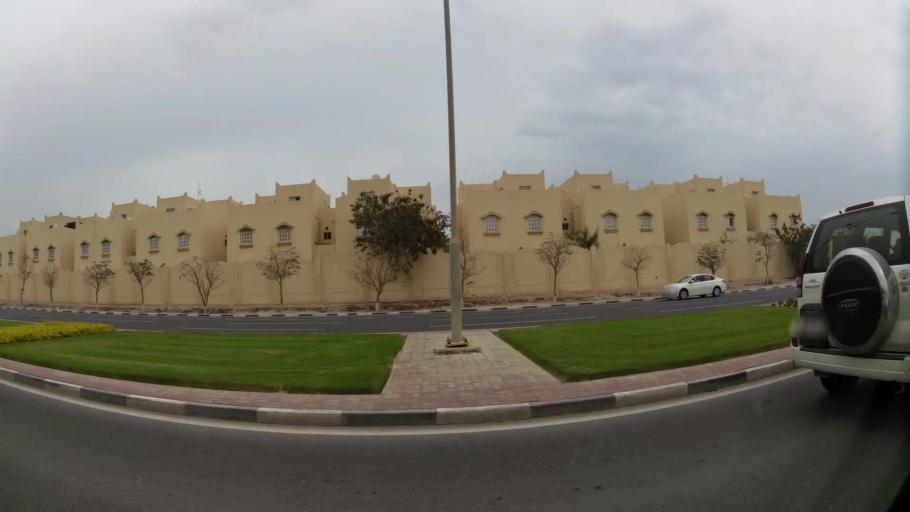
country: QA
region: Baladiyat ad Dawhah
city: Doha
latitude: 25.3289
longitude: 51.4836
